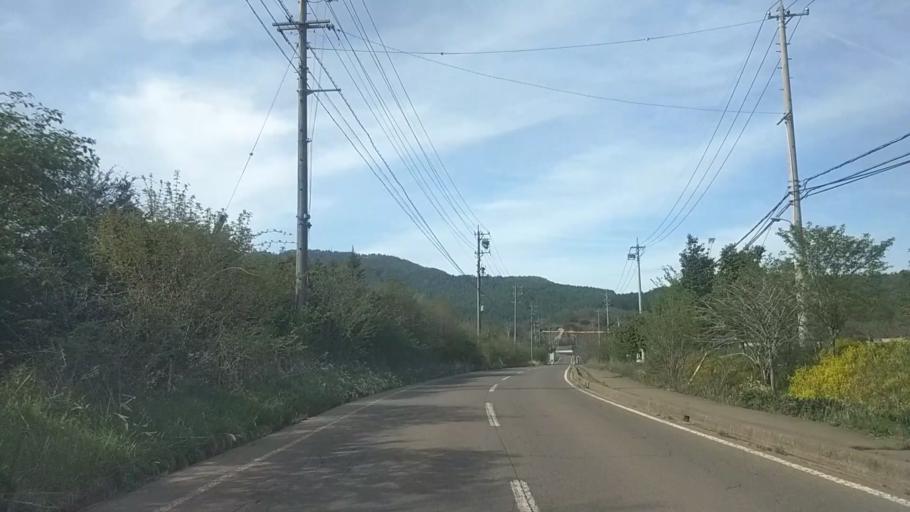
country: JP
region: Yamanashi
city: Nirasaki
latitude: 35.9432
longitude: 138.4684
